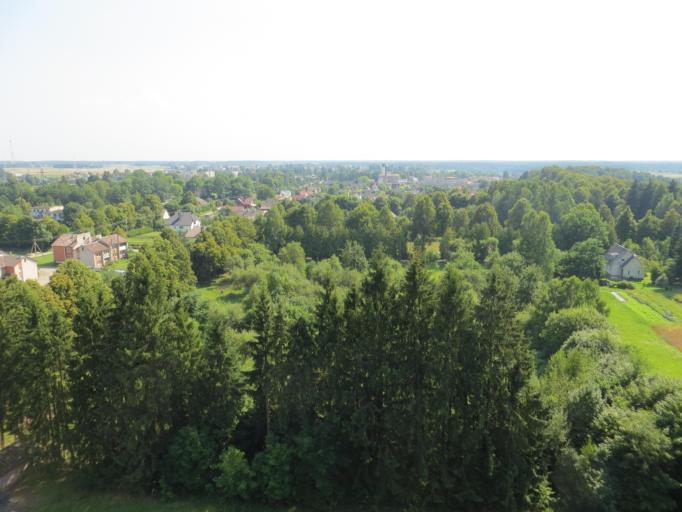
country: LT
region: Alytaus apskritis
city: Druskininkai
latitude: 54.1023
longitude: 23.8554
